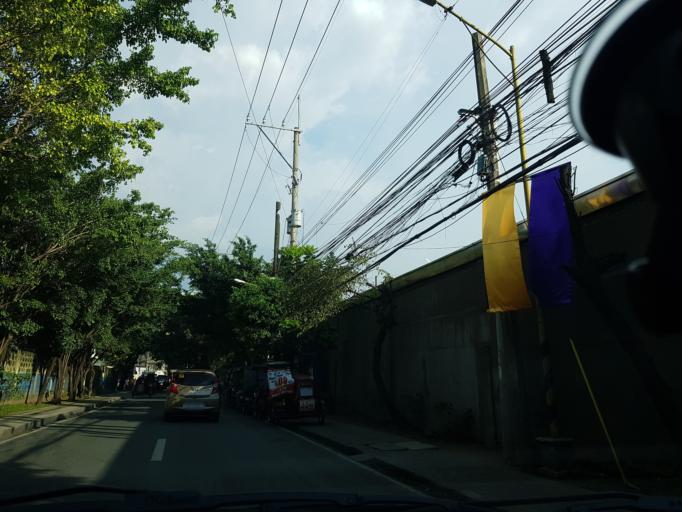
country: PH
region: Metro Manila
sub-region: Marikina
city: Calumpang
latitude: 14.6105
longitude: 121.0904
